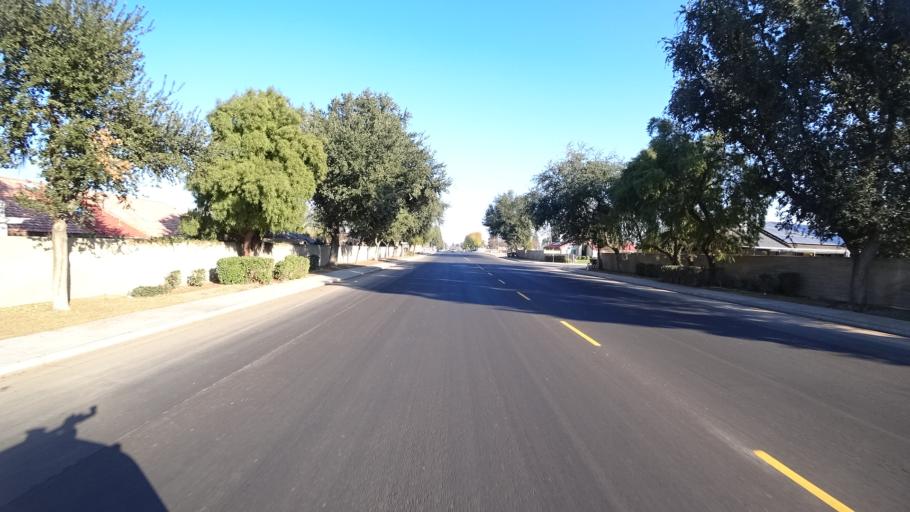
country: US
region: California
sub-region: Kern County
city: Greenacres
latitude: 35.3252
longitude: -119.0980
